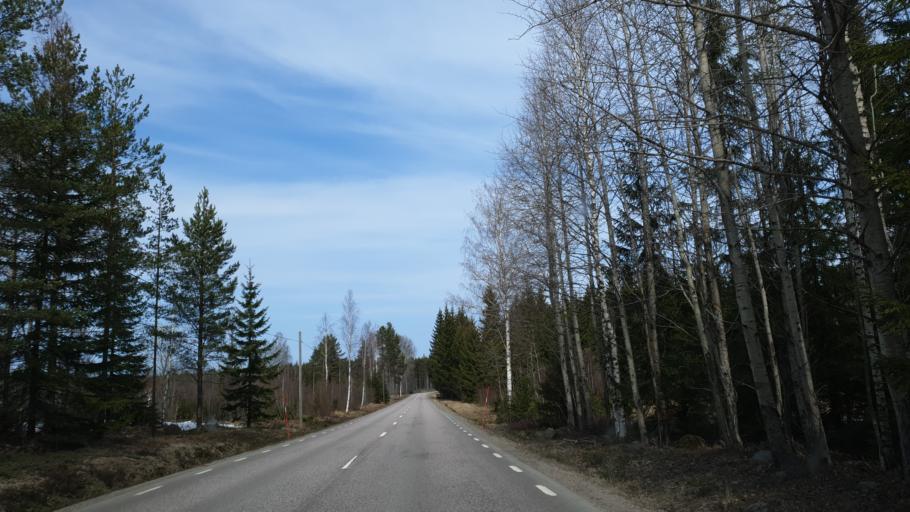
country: SE
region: Gaevleborg
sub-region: Gavle Kommun
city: Norrsundet
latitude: 60.9888
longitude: 17.0798
